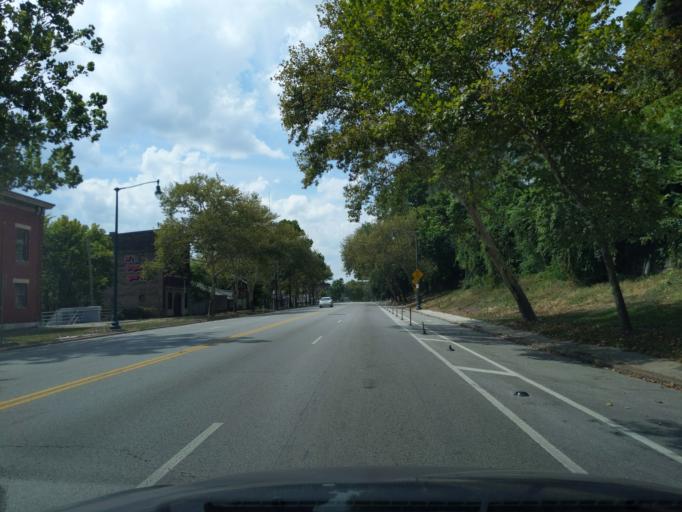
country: US
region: Kentucky
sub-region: Kenton County
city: Ludlow
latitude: 39.1213
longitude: -84.5281
